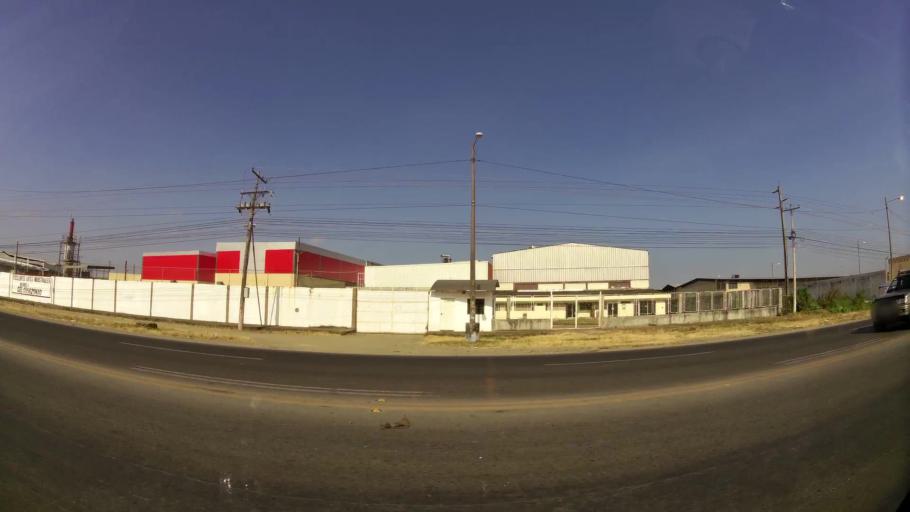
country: EC
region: Guayas
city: Eloy Alfaro
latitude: -2.1935
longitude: -79.8226
